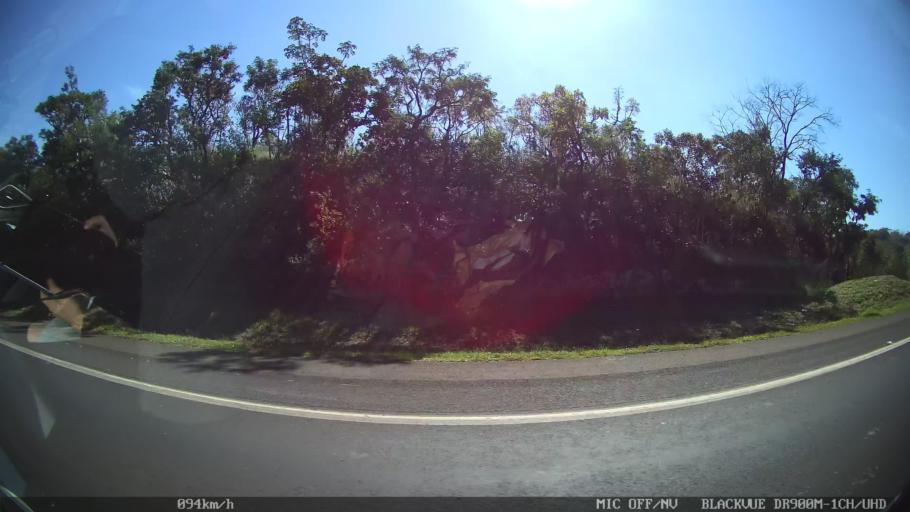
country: BR
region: Sao Paulo
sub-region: Franca
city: Franca
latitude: -20.5560
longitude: -47.4345
